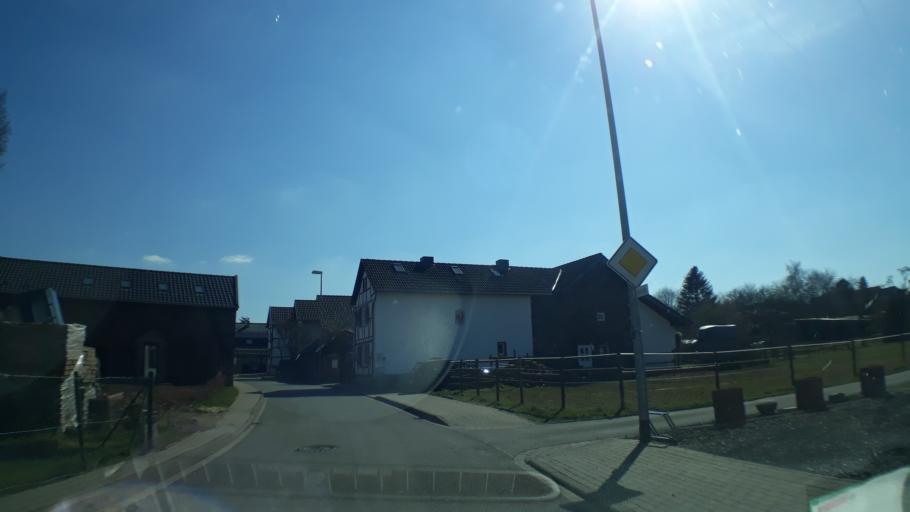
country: DE
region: North Rhine-Westphalia
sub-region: Regierungsbezirk Koln
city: Mechernich
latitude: 50.5698
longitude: 6.6492
